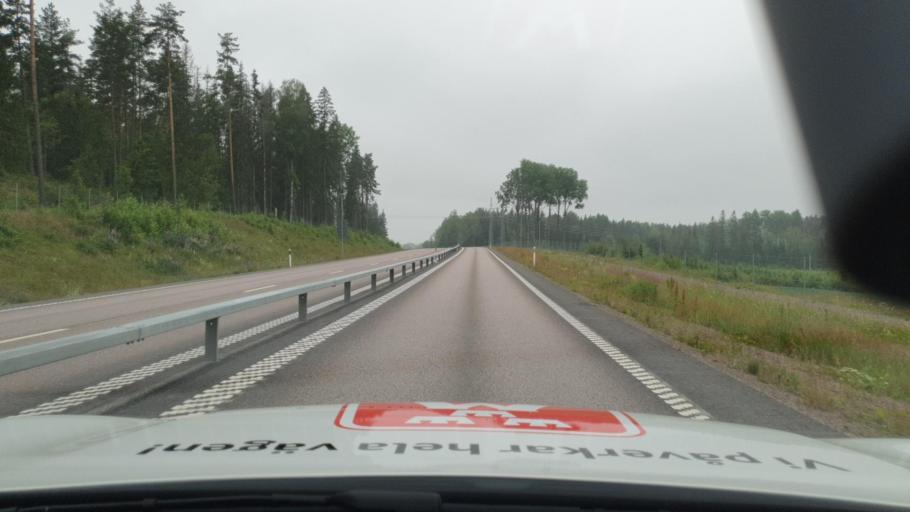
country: SE
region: Vaermland
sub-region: Karlstads Kommun
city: Edsvalla
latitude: 59.5414
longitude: 13.2016
